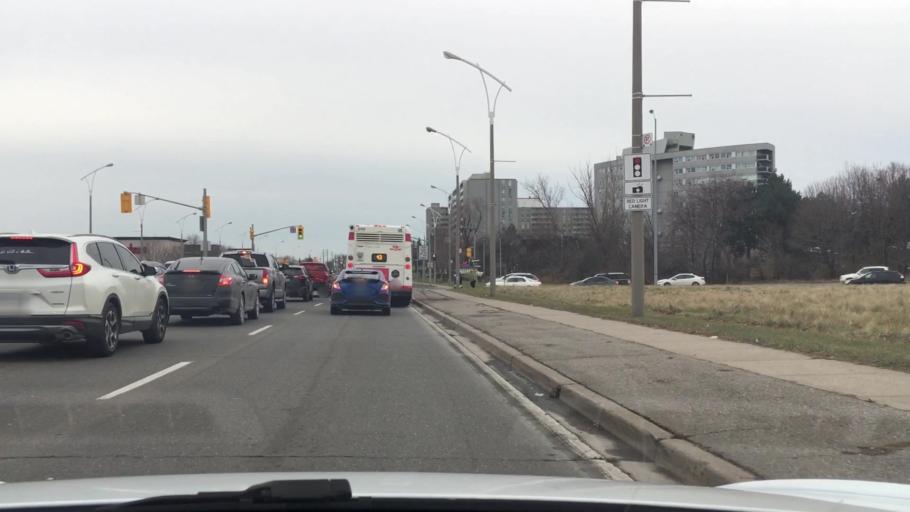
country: CA
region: Ontario
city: Scarborough
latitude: 43.7738
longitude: -79.2842
